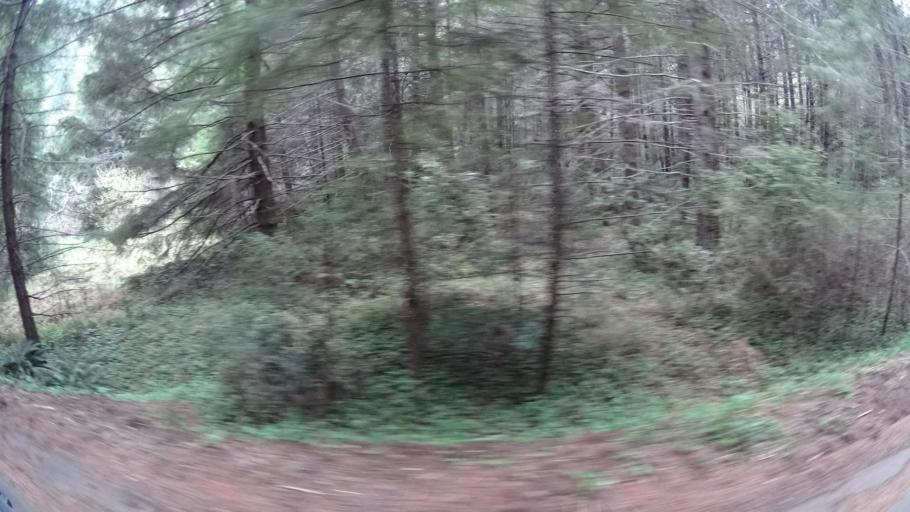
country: US
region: California
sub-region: Humboldt County
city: Redway
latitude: 40.0207
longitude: -124.0048
